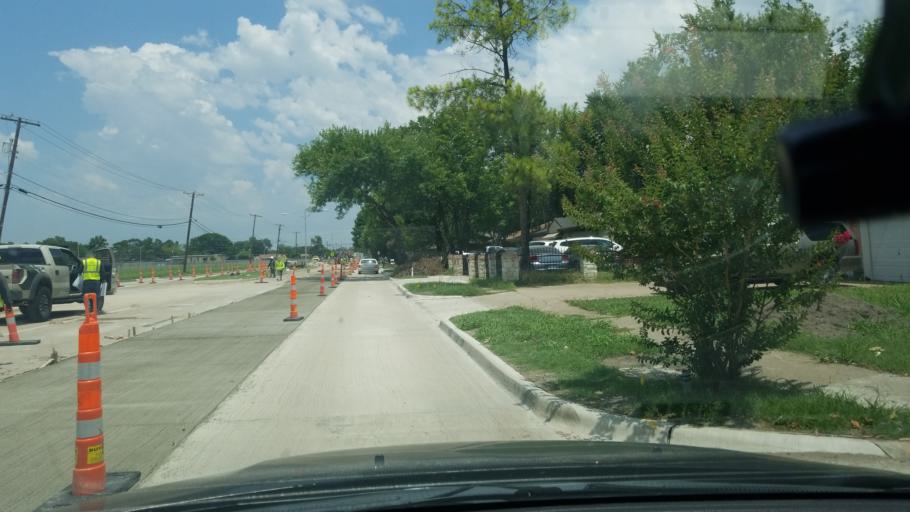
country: US
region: Texas
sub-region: Dallas County
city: Balch Springs
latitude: 32.7433
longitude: -96.6655
